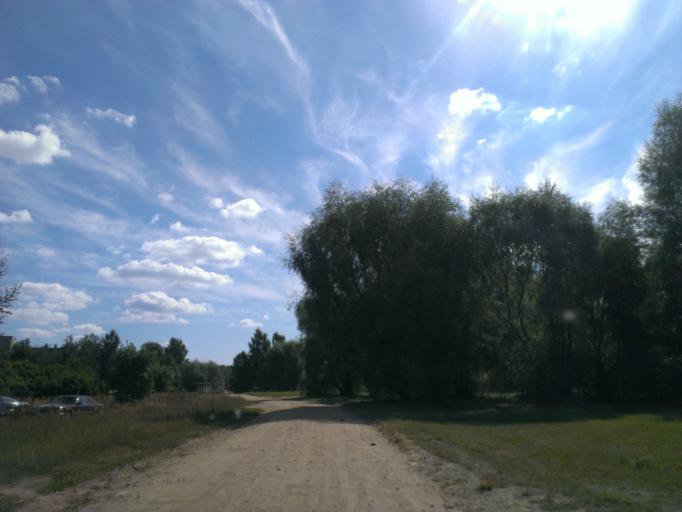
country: LV
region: Adazi
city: Adazi
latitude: 57.0794
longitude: 24.3245
